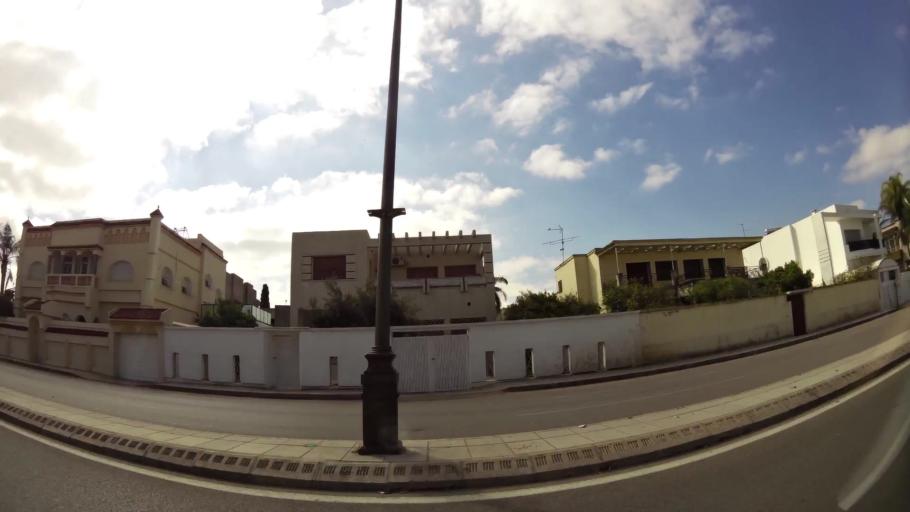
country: MA
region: Fes-Boulemane
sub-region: Fes
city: Fes
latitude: 34.0307
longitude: -5.0149
